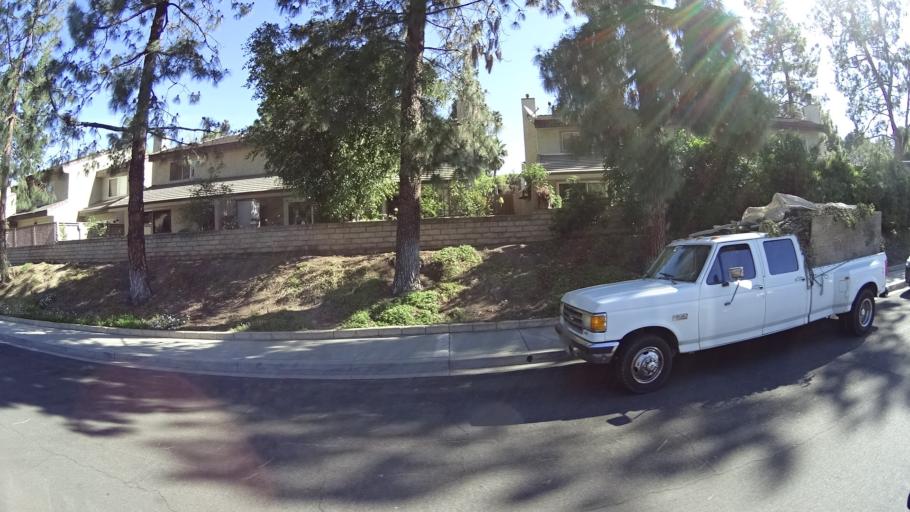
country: US
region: California
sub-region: Ventura County
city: Thousand Oaks
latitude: 34.2196
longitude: -118.8525
